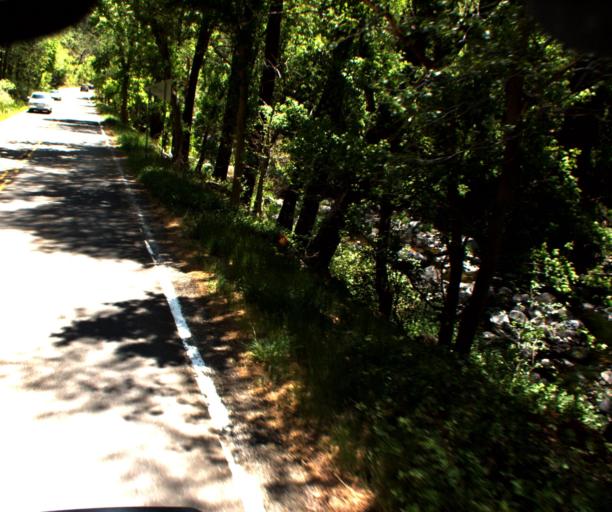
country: US
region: Arizona
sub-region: Coconino County
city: Kachina Village
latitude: 35.0066
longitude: -111.7354
